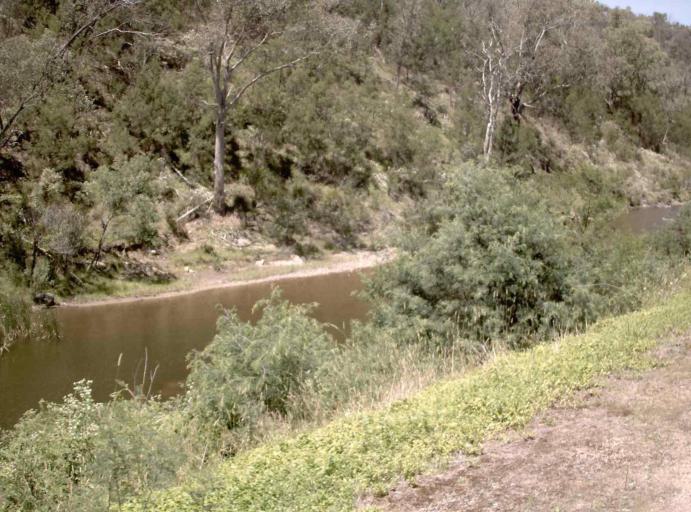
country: AU
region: Victoria
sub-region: East Gippsland
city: Bairnsdale
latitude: -37.4394
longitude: 147.8334
